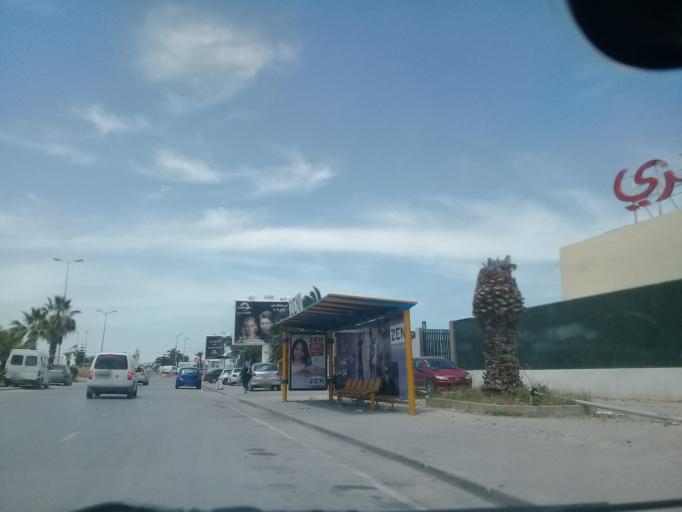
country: TN
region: Ariana
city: Ariana
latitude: 36.8383
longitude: 10.2375
